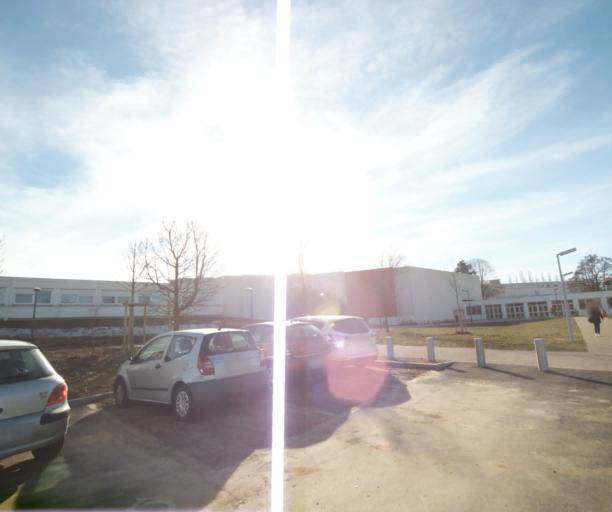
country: FR
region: Lorraine
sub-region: Departement de Meurthe-et-Moselle
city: Villers-les-Nancy
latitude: 48.6500
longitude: 6.1420
